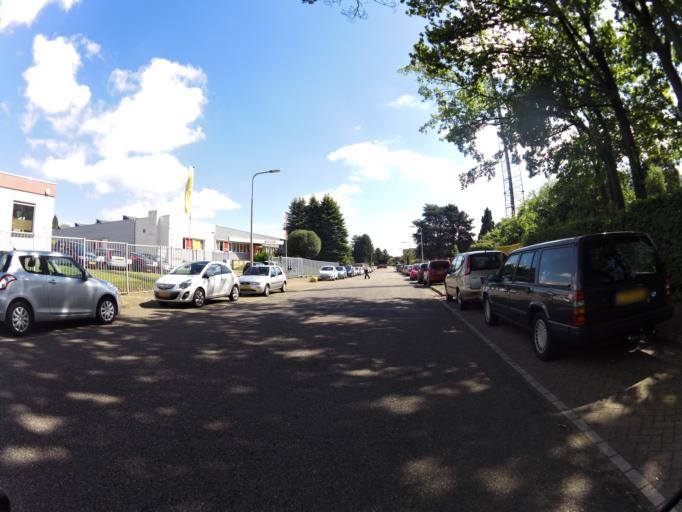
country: NL
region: Limburg
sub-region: Gemeente Kerkrade
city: Kerkrade
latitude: 50.8617
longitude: 6.0391
